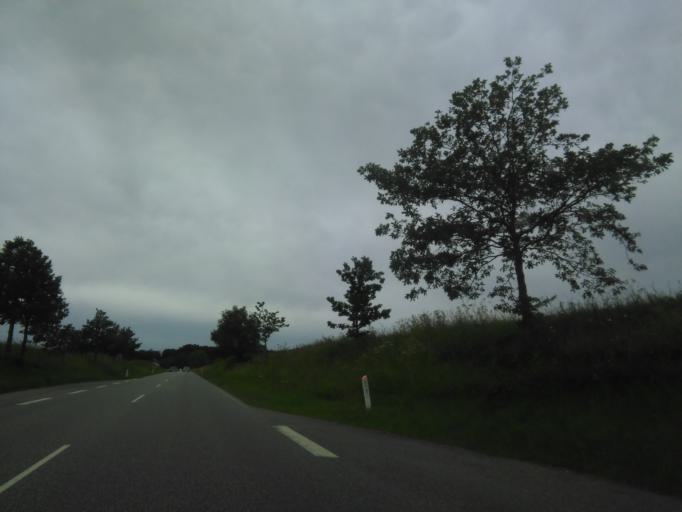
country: DK
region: Central Jutland
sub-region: Skanderborg Kommune
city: Skanderborg
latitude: 55.9577
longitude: 9.9847
